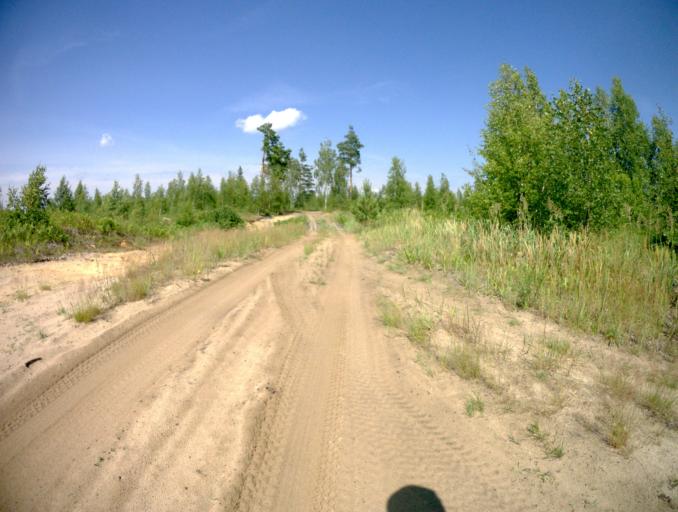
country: RU
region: Ivanovo
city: Talitsy
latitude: 56.4699
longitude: 42.2239
